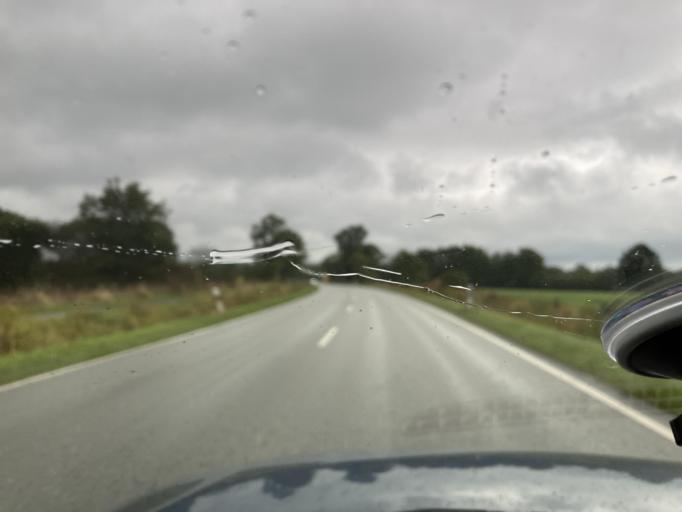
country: DE
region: Schleswig-Holstein
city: Welmbuttel
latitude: 54.2070
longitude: 9.2651
